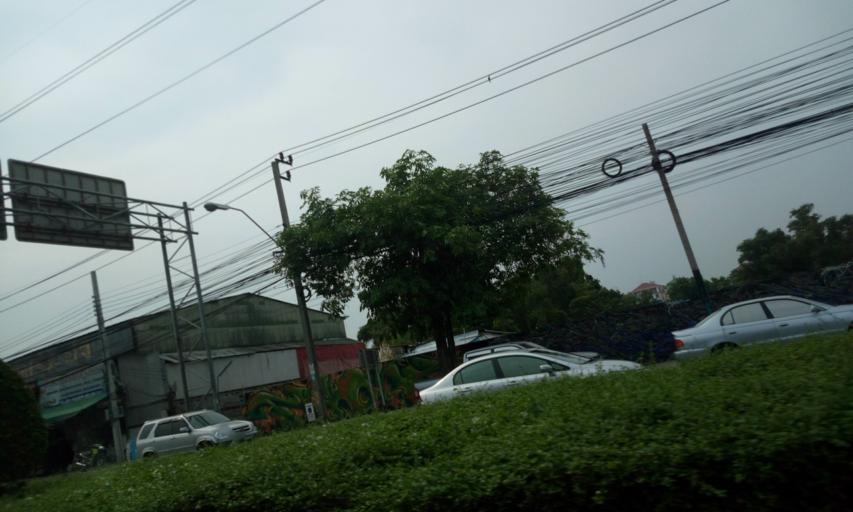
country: TH
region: Bangkok
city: Lat Krabang
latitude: 13.7217
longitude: 100.7705
